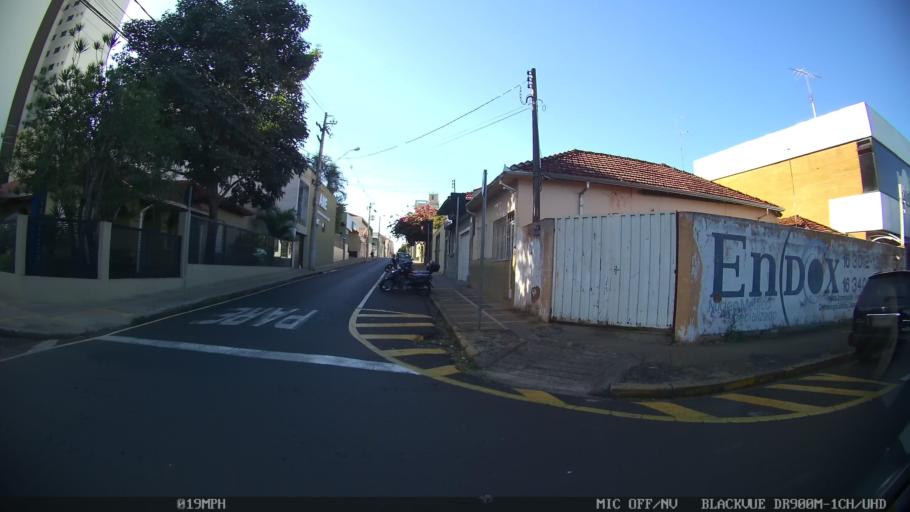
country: BR
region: Sao Paulo
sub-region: Franca
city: Franca
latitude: -20.5412
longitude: -47.4040
